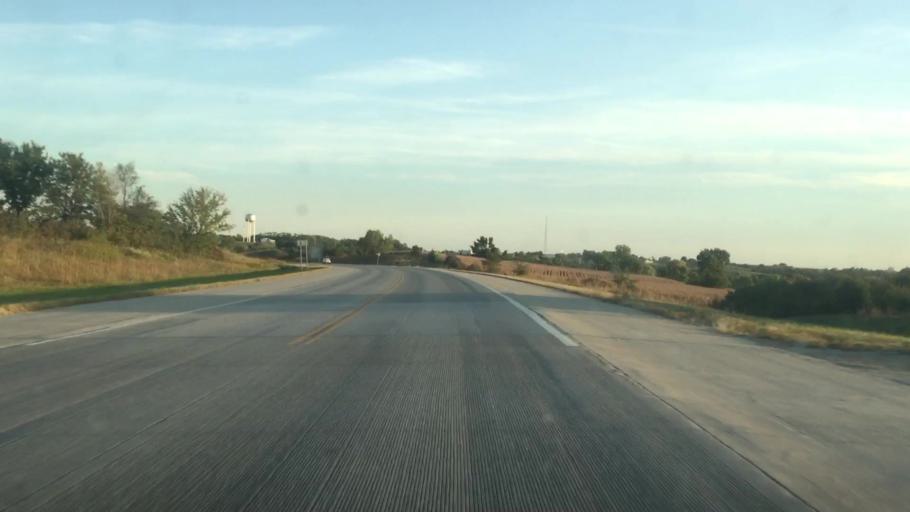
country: US
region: Kansas
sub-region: Leavenworth County
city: Leavenworth
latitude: 39.3798
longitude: -95.0574
